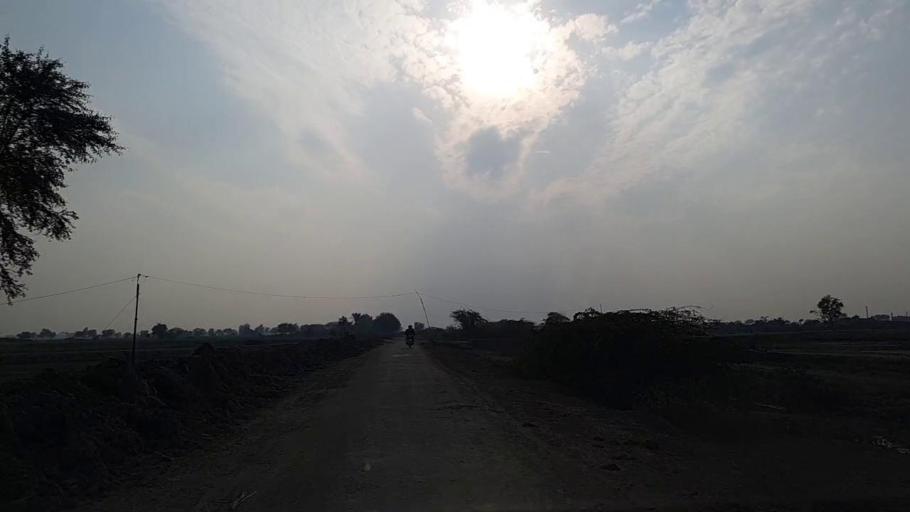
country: PK
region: Sindh
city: Jam Sahib
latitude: 26.3072
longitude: 68.5207
